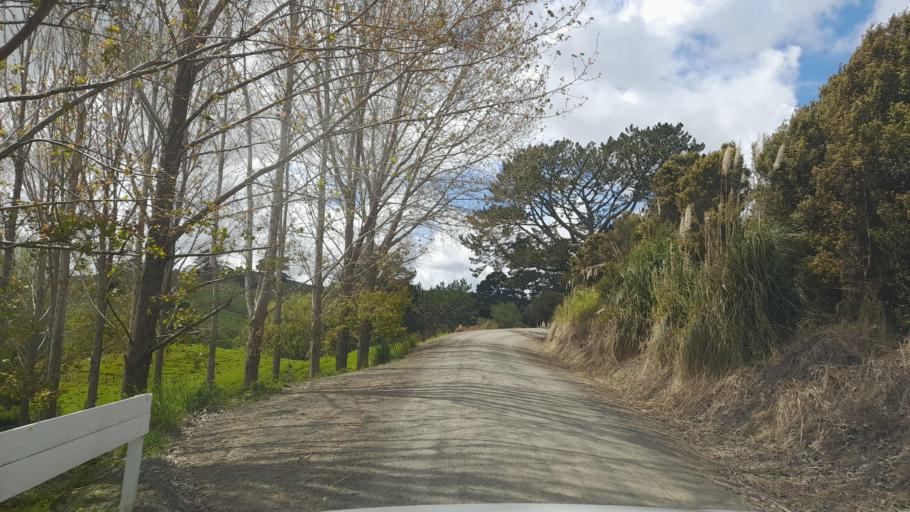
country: NZ
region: Auckland
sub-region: Auckland
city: Wellsford
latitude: -36.1826
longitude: 174.3180
